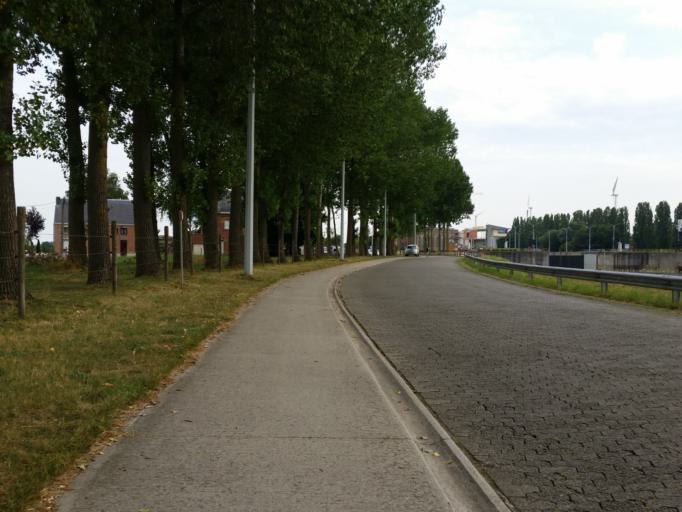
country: BE
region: Flanders
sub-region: Provincie Vlaams-Brabant
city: Kapelle-op-den-Bos
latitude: 51.0027
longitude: 4.3712
